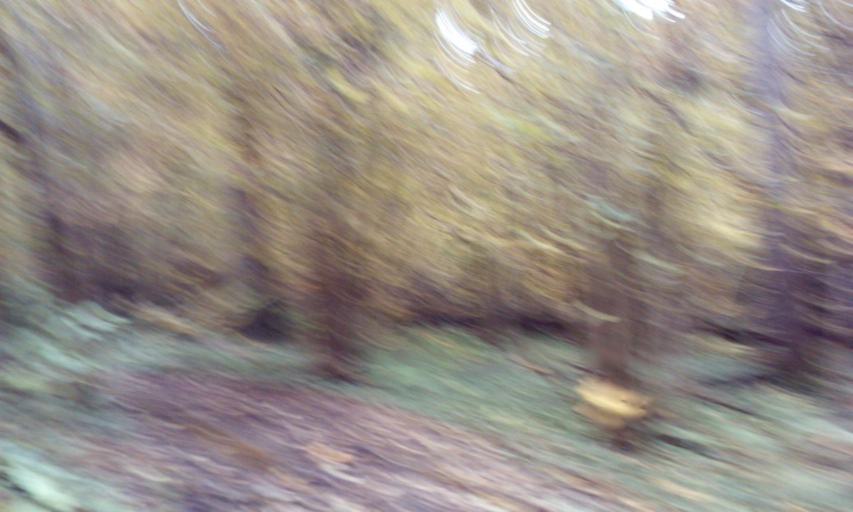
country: RU
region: Moskovskaya
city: Gorki Vtoryye
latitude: 55.6938
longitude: 37.1750
